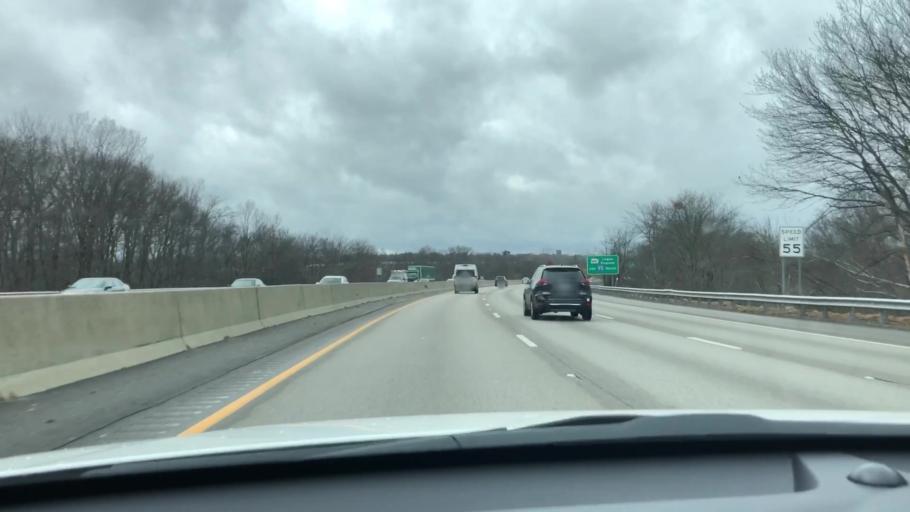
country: US
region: Massachusetts
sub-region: Norfolk County
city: Braintree
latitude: 42.2050
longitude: -70.9907
